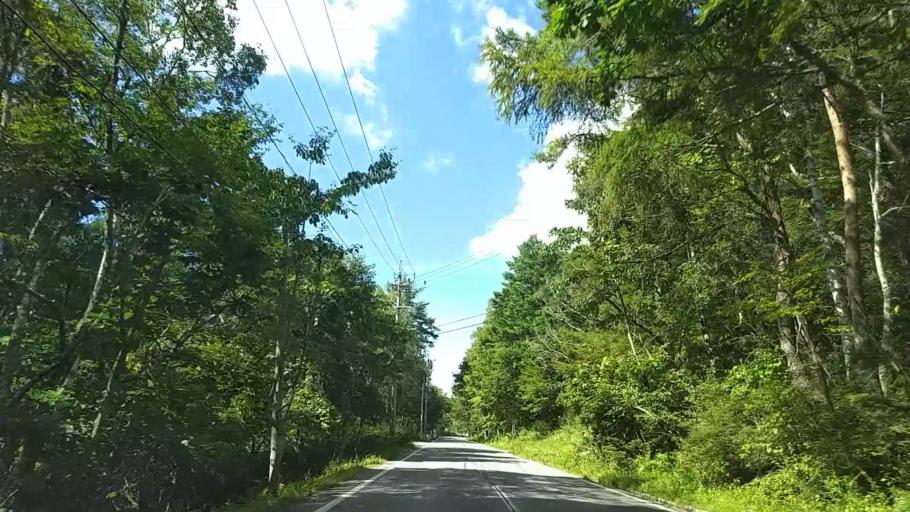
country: JP
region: Nagano
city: Chino
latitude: 36.1264
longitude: 138.2721
